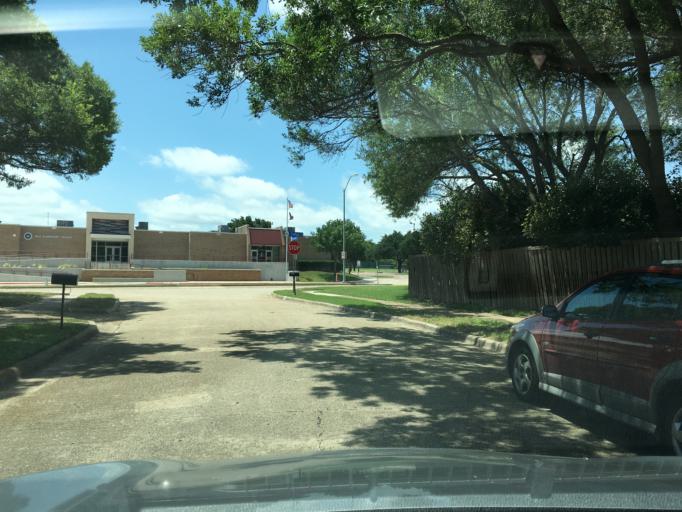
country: US
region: Texas
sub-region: Dallas County
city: Richardson
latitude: 32.9683
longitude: -96.6900
